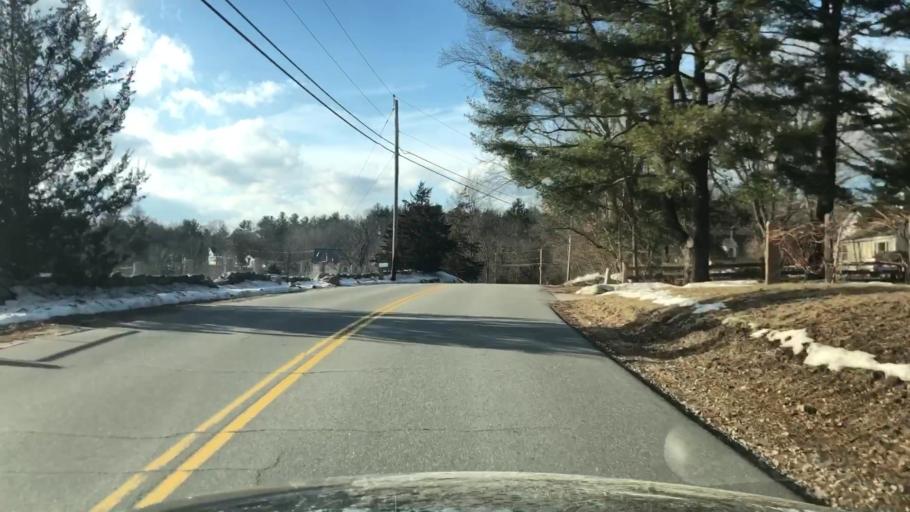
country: US
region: New Hampshire
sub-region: Hillsborough County
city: Milford
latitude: 42.8487
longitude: -71.6764
